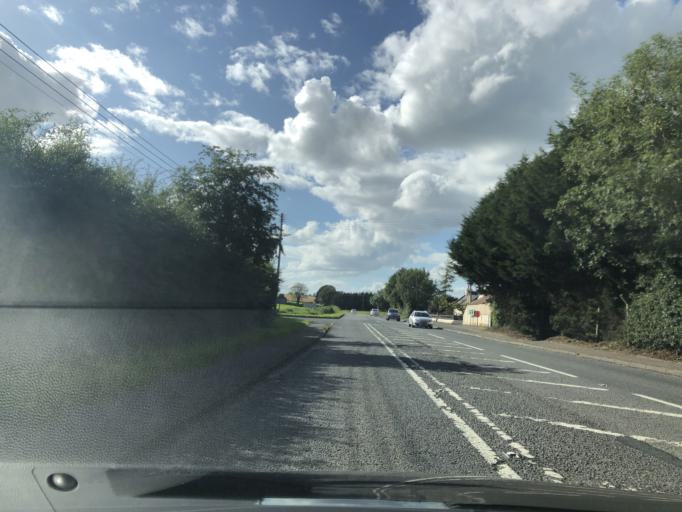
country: GB
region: Northern Ireland
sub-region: Ards District
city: Comber
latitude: 54.5693
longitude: -5.7712
